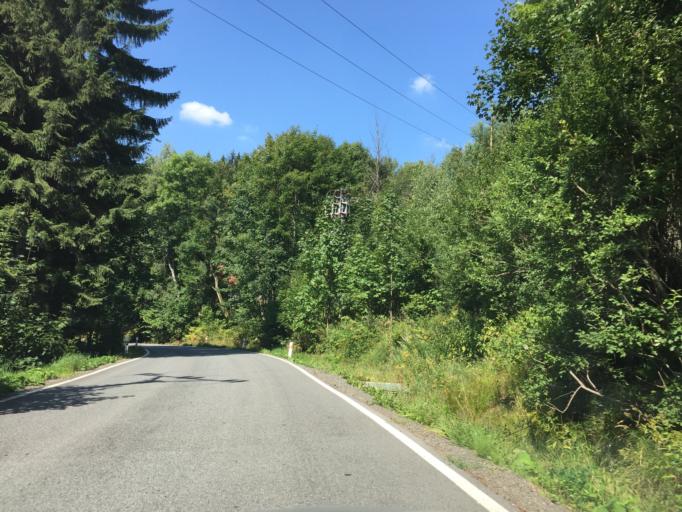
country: CZ
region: Liberecky
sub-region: Okres Jablonec nad Nisou
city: Janov nad Nisou
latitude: 50.7838
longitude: 15.1816
